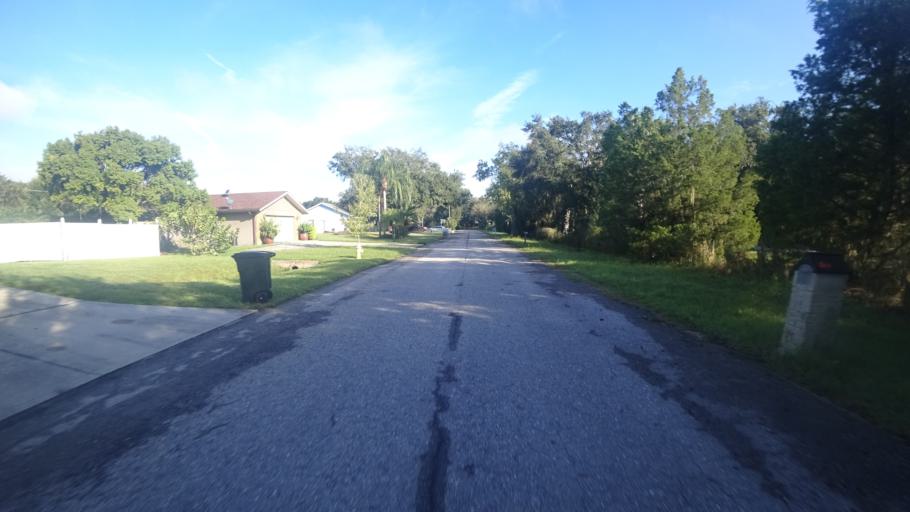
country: US
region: Florida
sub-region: Manatee County
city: Ellenton
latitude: 27.5524
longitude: -82.4623
